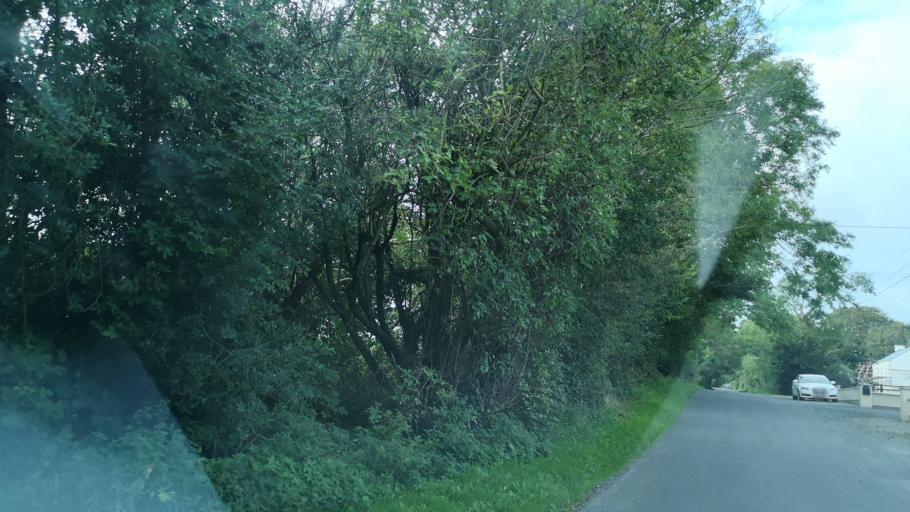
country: IE
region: Connaught
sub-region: County Galway
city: Ballinasloe
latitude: 53.3187
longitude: -8.1041
